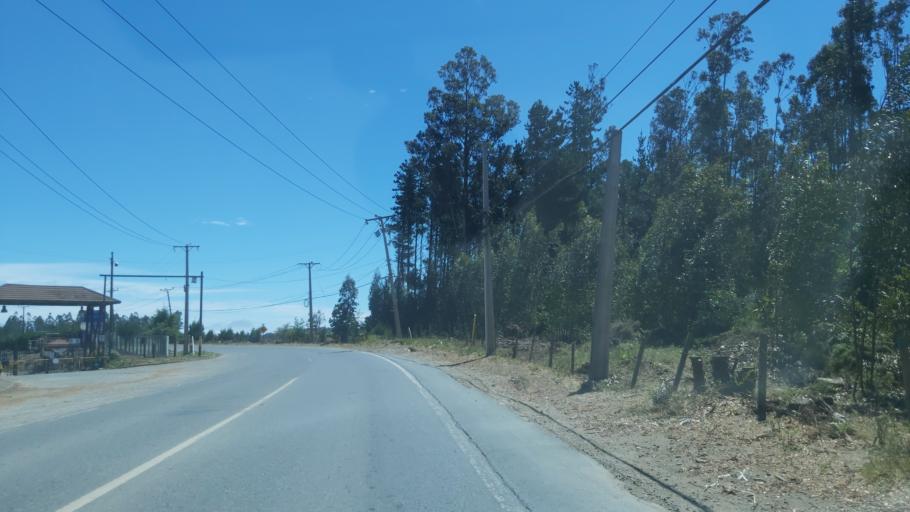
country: CL
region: Maule
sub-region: Provincia de Talca
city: Constitucion
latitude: -35.3675
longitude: -72.4081
